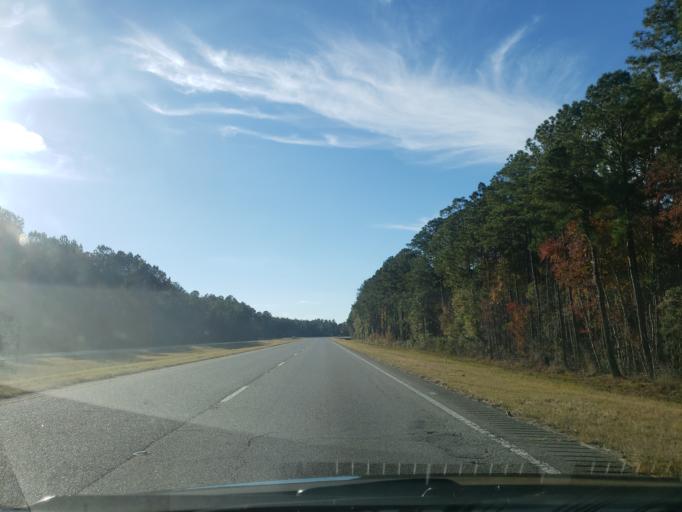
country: US
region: Georgia
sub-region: Ware County
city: Deenwood
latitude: 31.2096
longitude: -82.4064
